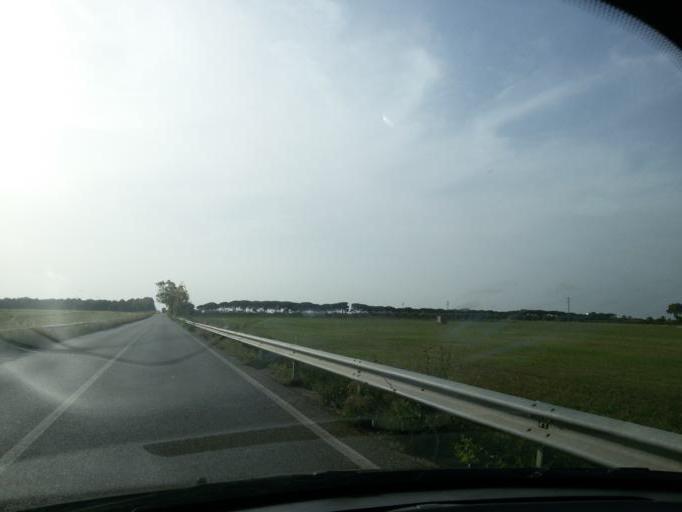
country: IT
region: Apulia
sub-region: Provincia di Lecce
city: Porto Cesareo
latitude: 40.2785
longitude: 17.8926
